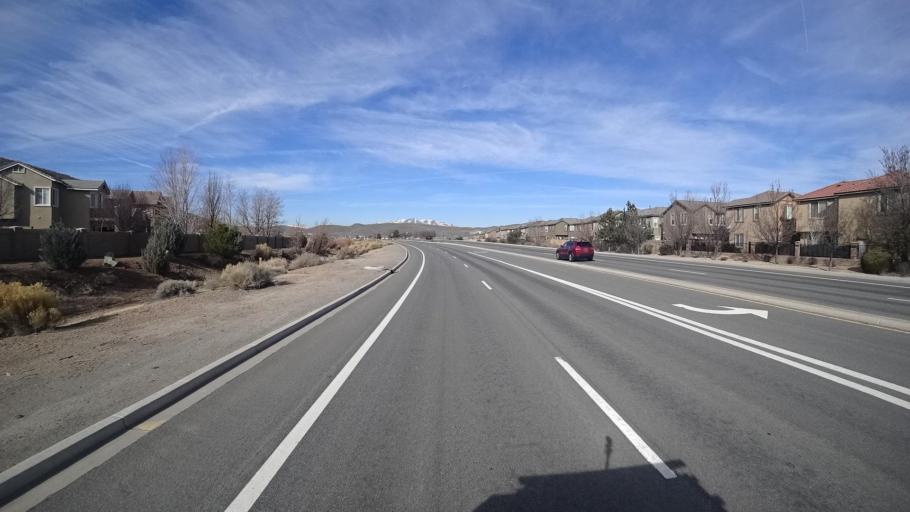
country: US
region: Nevada
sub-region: Washoe County
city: Spanish Springs
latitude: 39.6068
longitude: -119.7009
